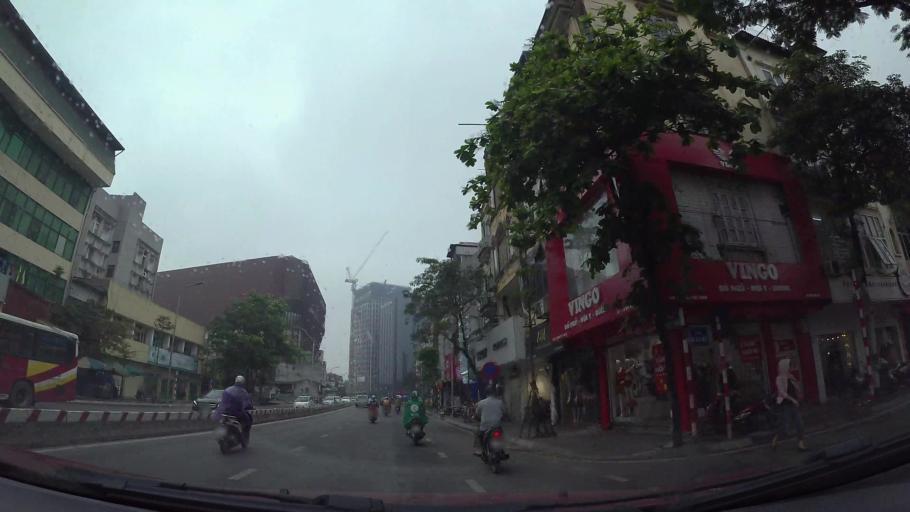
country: VN
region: Ha Noi
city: Dong Da
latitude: 21.0075
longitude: 105.8328
